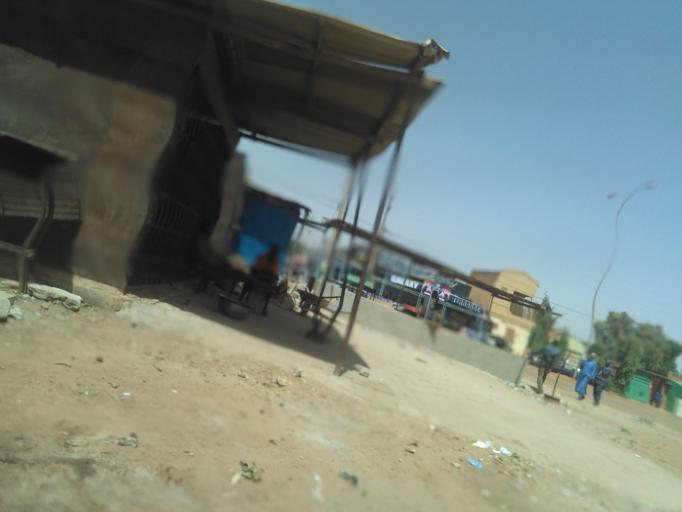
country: BF
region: Centre
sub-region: Kadiogo Province
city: Ouagadougou
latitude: 12.3907
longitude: -1.5614
